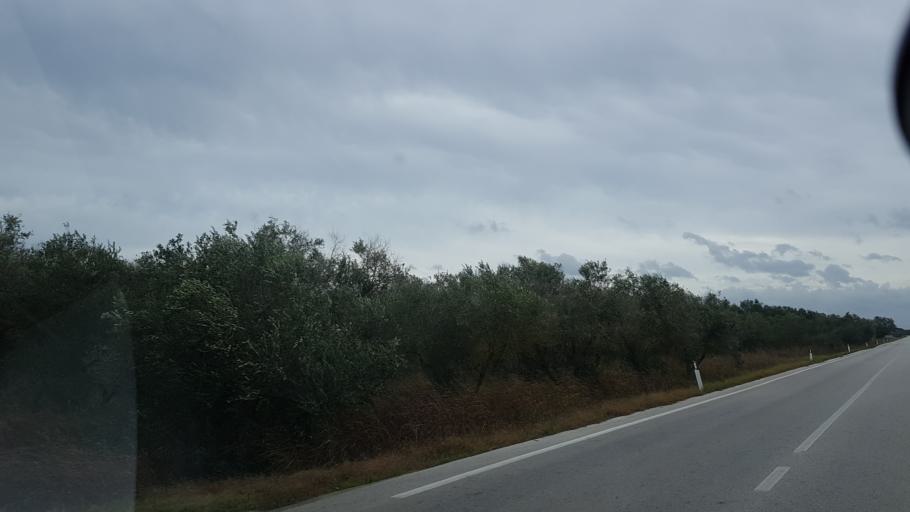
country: IT
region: Apulia
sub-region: Provincia di Lecce
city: Guagnano
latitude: 40.4009
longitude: 17.9122
